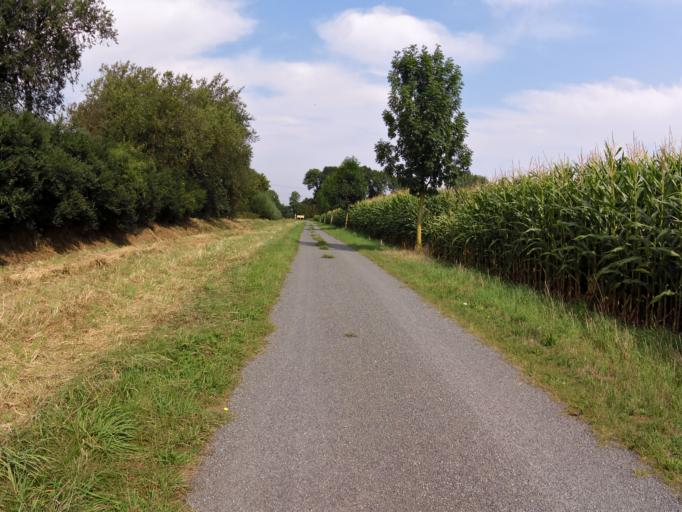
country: DE
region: Lower Saxony
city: Stolzenau
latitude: 52.5326
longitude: 9.0803
